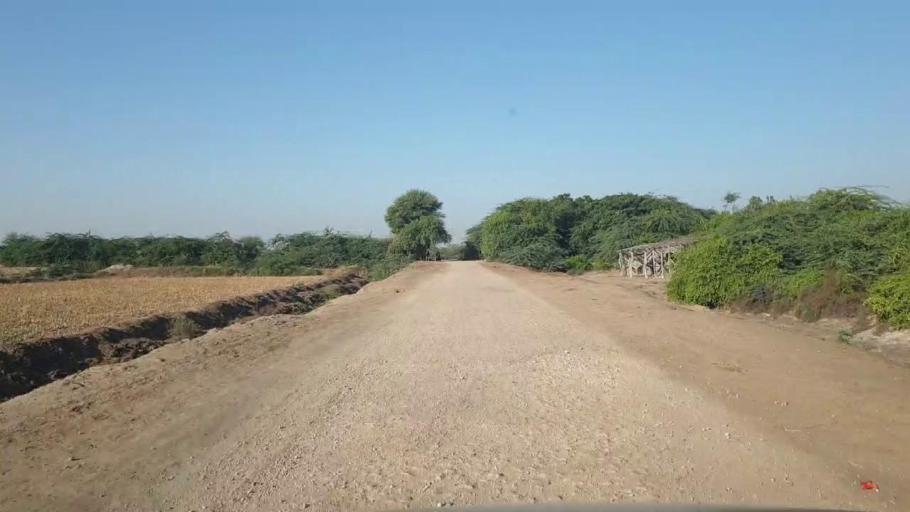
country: PK
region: Sindh
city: Badin
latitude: 24.6870
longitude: 68.8178
